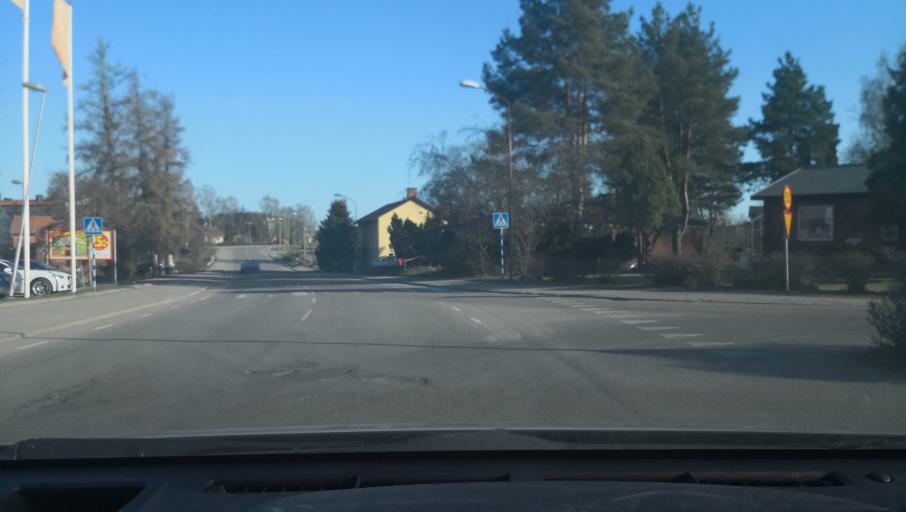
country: SE
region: Uppsala
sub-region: Heby Kommun
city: Heby
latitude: 59.9383
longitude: 16.8656
